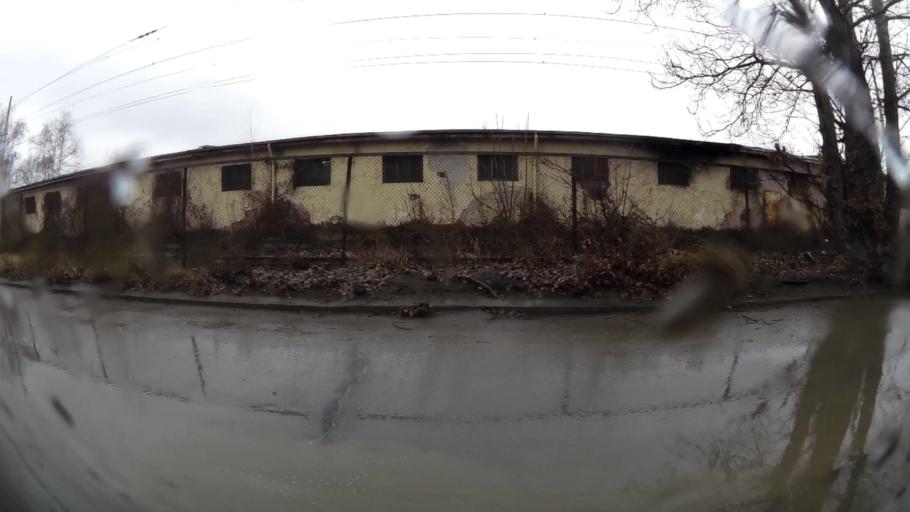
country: BG
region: Sofia-Capital
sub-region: Stolichna Obshtina
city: Sofia
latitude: 42.6578
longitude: 23.4148
